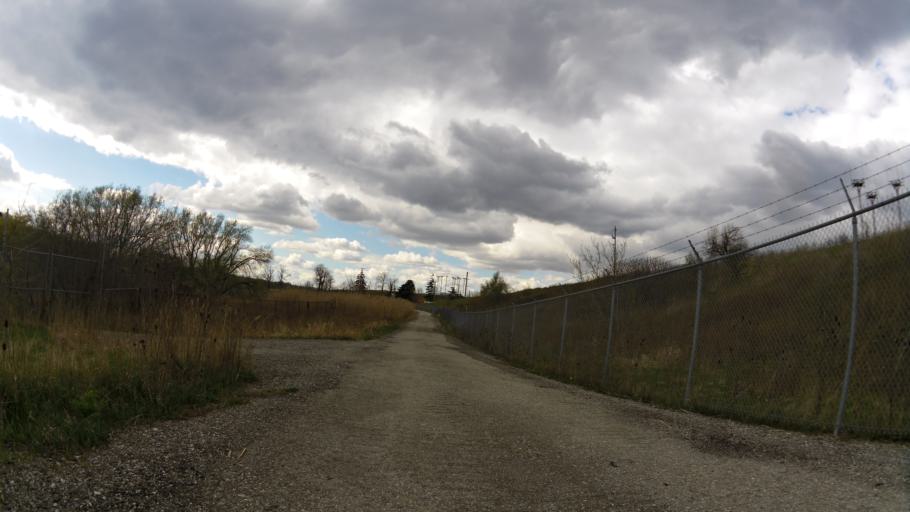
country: CA
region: Ontario
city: Etobicoke
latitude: 43.6630
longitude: -79.6309
